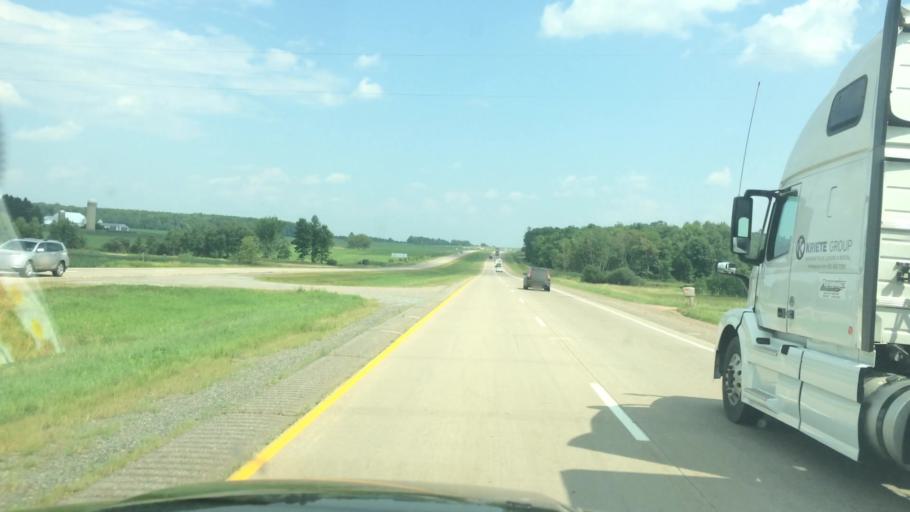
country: US
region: Wisconsin
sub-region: Marathon County
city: Athens
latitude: 44.9455
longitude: -90.1030
